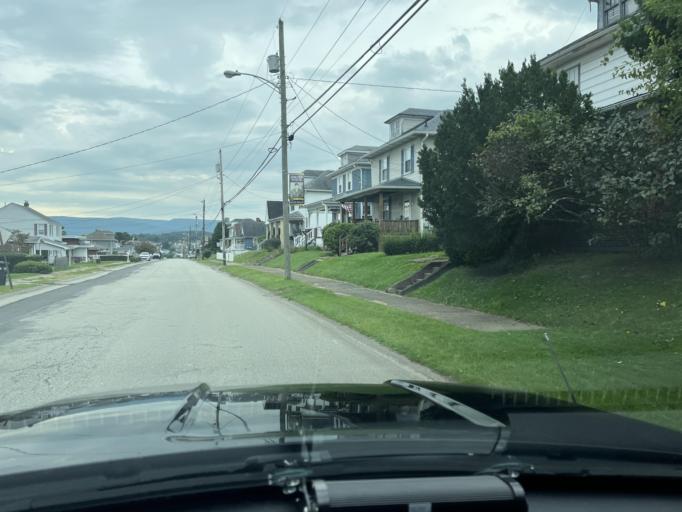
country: US
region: Pennsylvania
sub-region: Fayette County
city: South Uniontown
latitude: 39.9006
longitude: -79.7416
